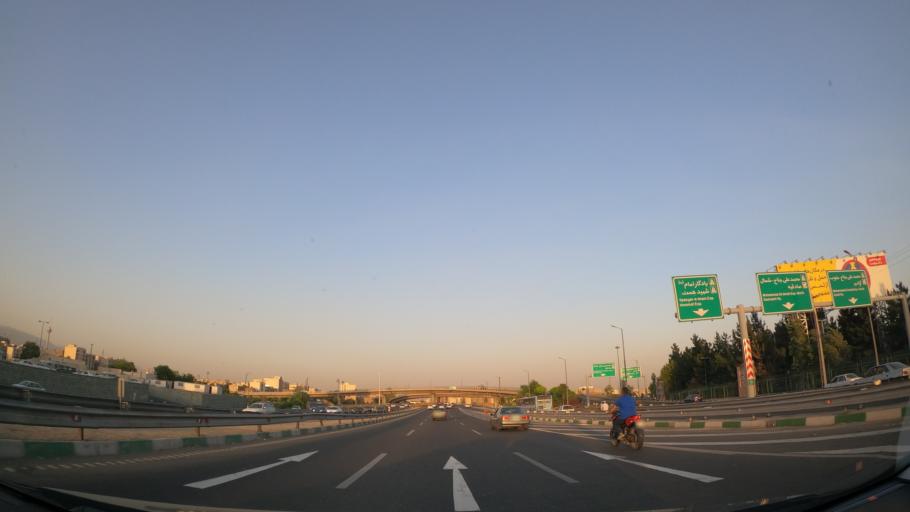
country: IR
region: Tehran
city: Tehran
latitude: 35.7128
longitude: 51.3332
